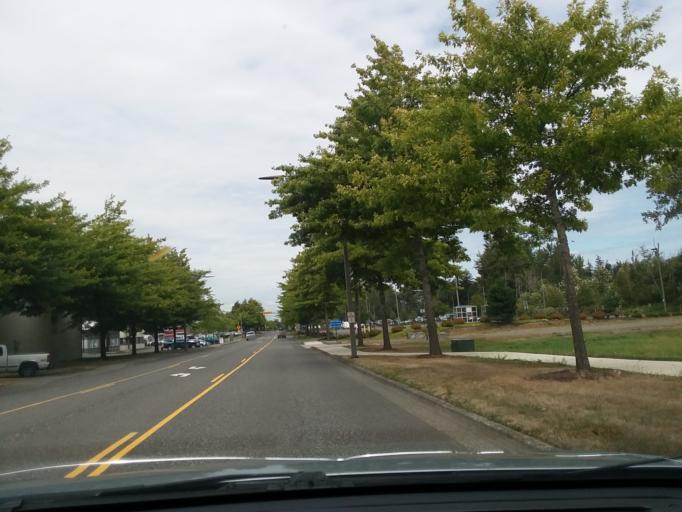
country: US
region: Washington
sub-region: Whatcom County
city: Marietta-Alderwood
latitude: 48.7913
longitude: -122.5306
